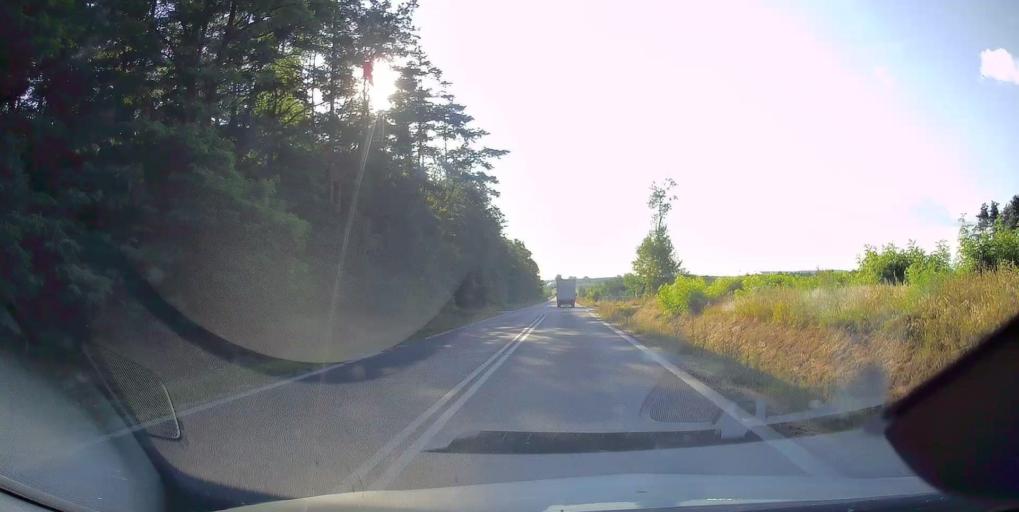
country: PL
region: Lodz Voivodeship
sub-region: Powiat rawski
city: Biala Rawska
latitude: 51.8006
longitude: 20.5141
